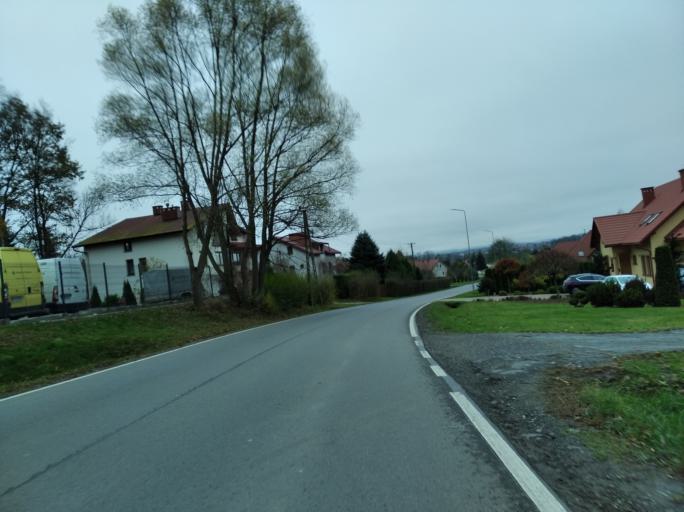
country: PL
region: Subcarpathian Voivodeship
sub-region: Krosno
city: Krosno
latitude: 49.7087
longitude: 21.7588
